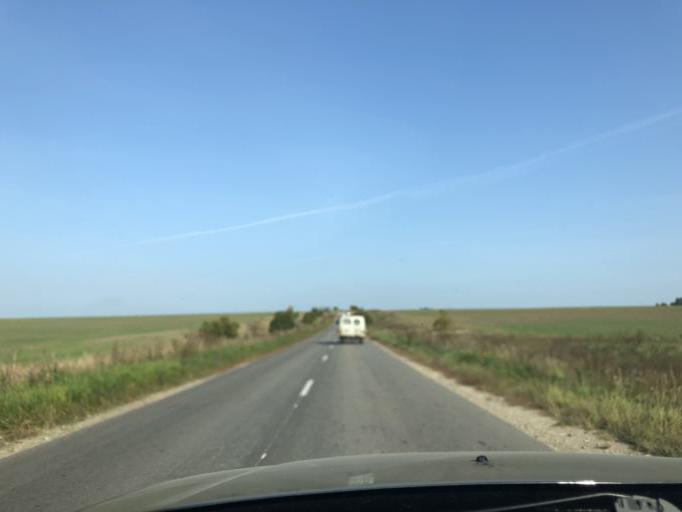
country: RU
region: Tula
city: Novogurovskiy
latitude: 54.3990
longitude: 37.3149
